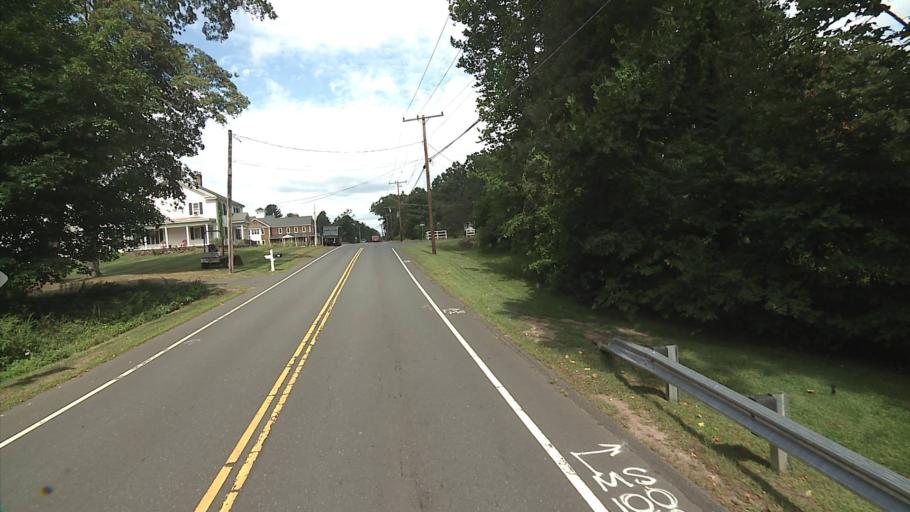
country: US
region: Connecticut
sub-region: Hartford County
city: Salmon Brook
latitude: 41.9407
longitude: -72.7754
